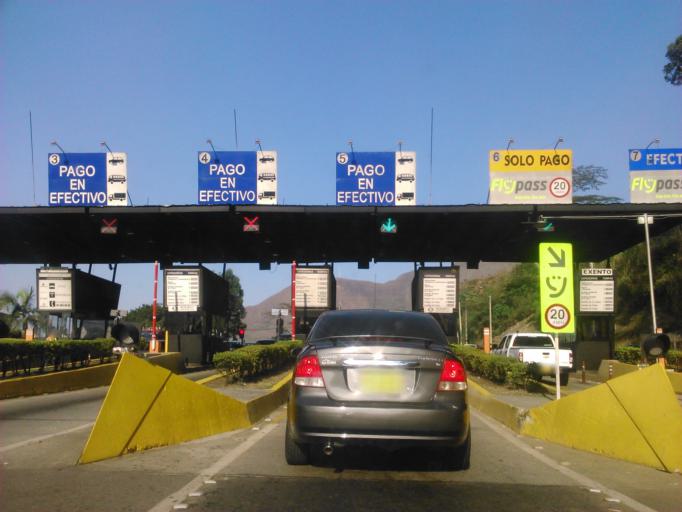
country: CO
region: Antioquia
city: Municipio de Copacabana
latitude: 6.3279
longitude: -75.5158
